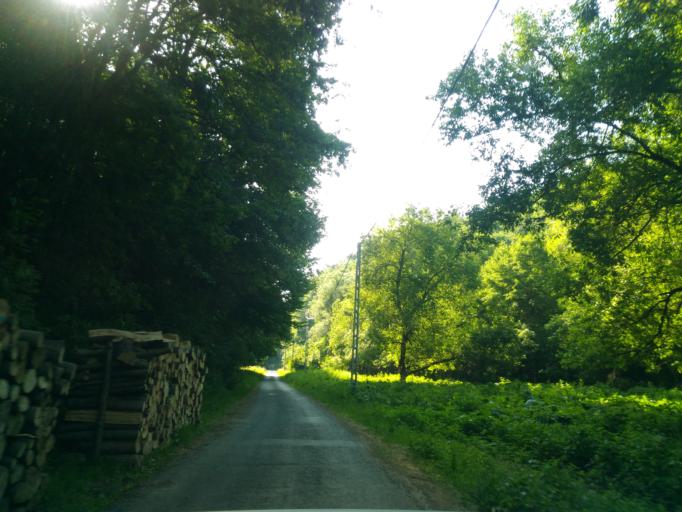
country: HU
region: Baranya
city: Komlo
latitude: 46.2304
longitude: 18.3156
